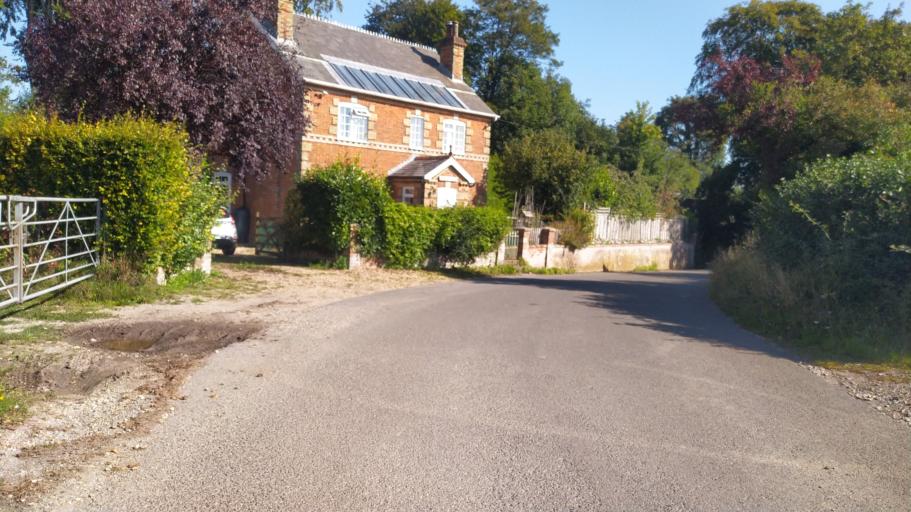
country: GB
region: England
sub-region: Hampshire
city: Abbotts Ann
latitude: 51.1728
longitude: -1.6047
